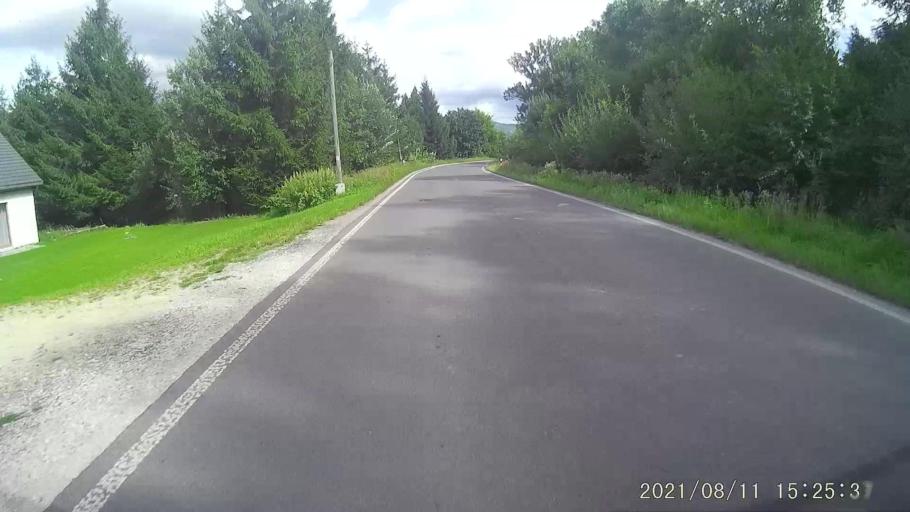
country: PL
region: Lower Silesian Voivodeship
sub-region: Powiat klodzki
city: Bystrzyca Klodzka
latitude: 50.2895
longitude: 16.6745
